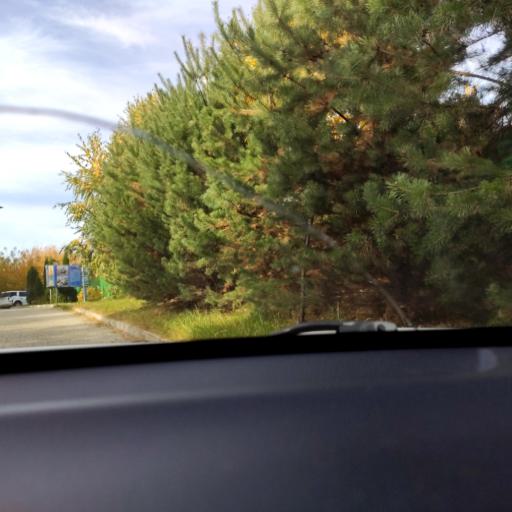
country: RU
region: Tatarstan
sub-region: Gorod Kazan'
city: Kazan
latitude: 55.8077
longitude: 49.0593
